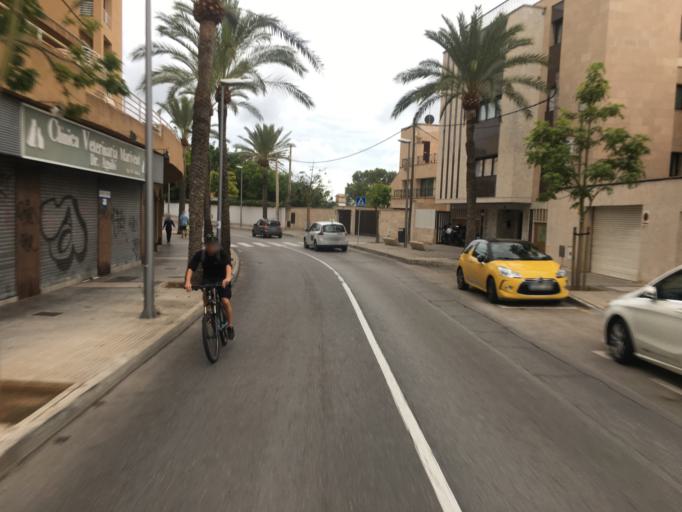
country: ES
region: Balearic Islands
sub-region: Illes Balears
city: Palma
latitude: 39.5517
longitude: 2.6088
